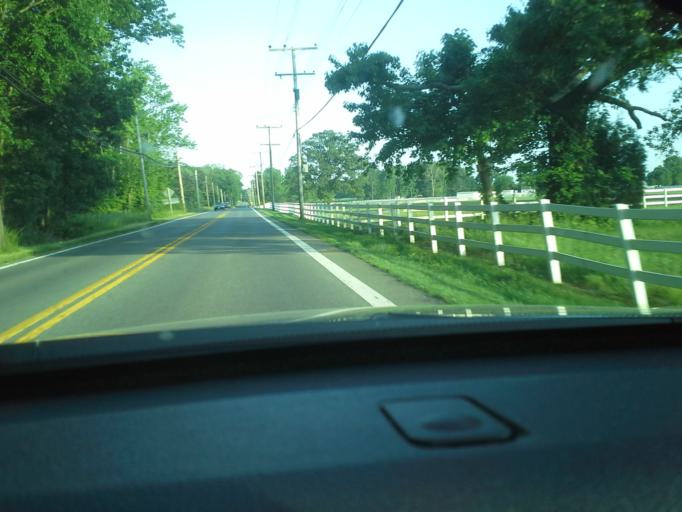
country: US
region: Maryland
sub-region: Anne Arundel County
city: Deale
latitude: 38.8246
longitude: -76.5609
